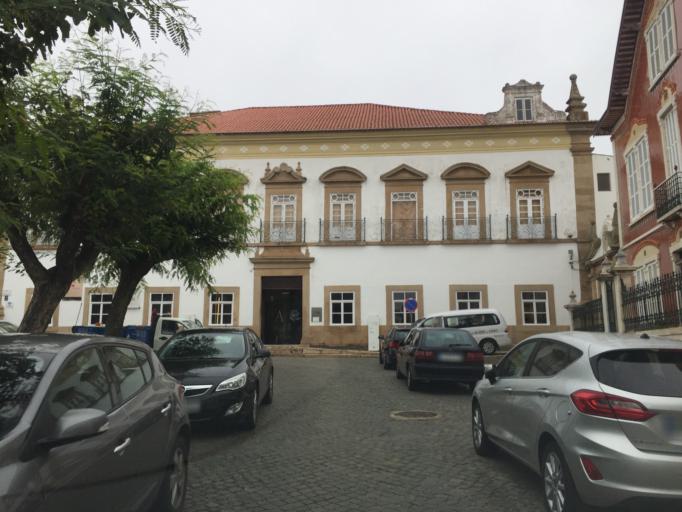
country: PT
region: Portalegre
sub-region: Alter do Chao
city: Alter do Chao
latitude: 39.1990
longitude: -7.6578
